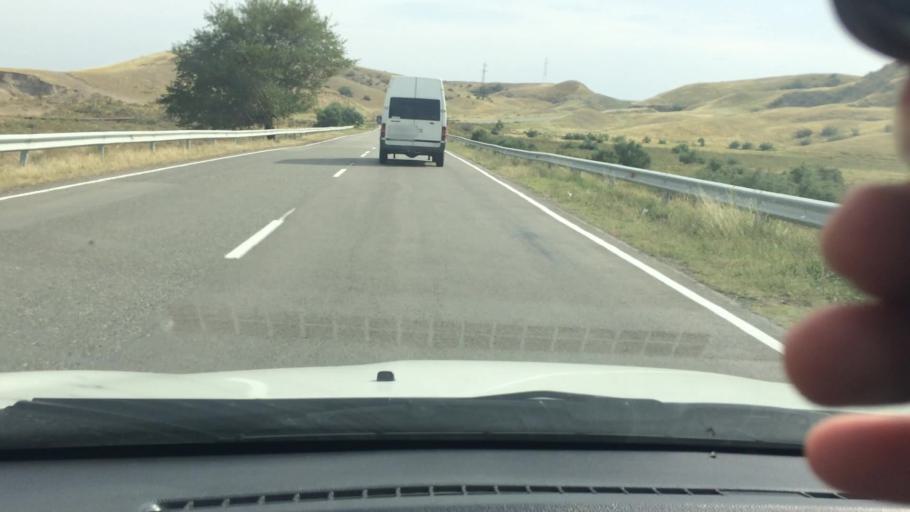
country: GE
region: Kvemo Kartli
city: Rust'avi
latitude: 41.5294
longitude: 44.9859
